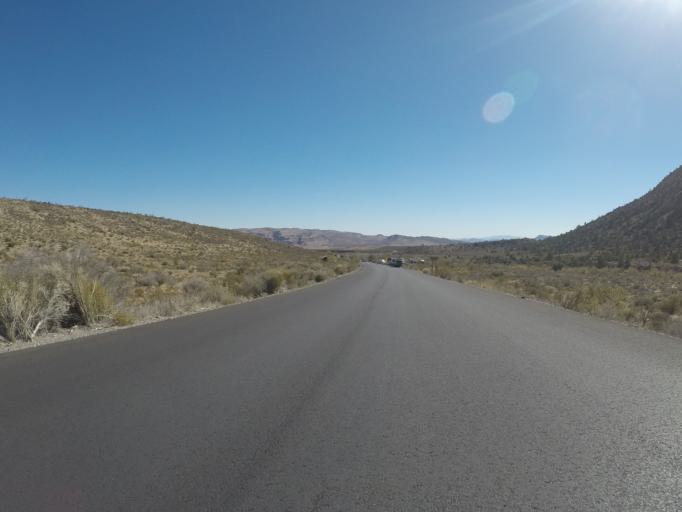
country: US
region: Nevada
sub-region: Clark County
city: Summerlin South
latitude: 36.1512
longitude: -115.4852
